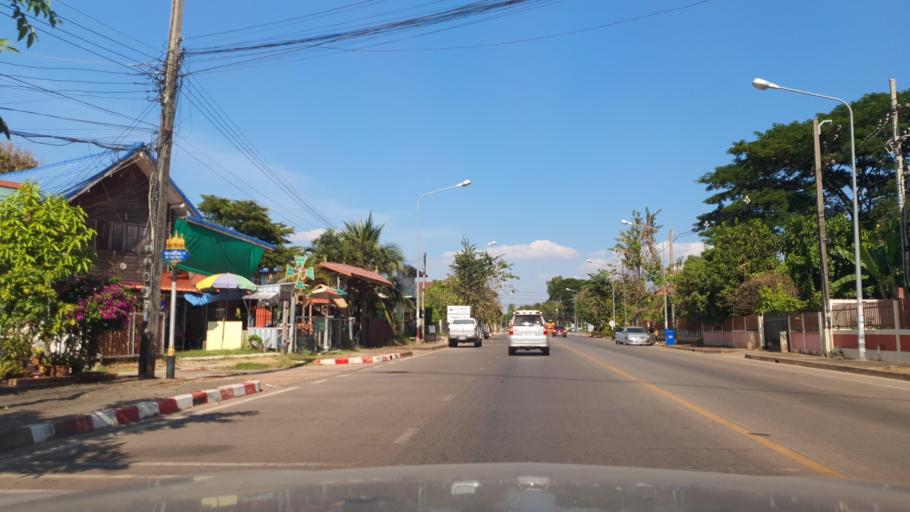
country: TH
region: Sakon Nakhon
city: Sakon Nakhon
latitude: 17.1597
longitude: 104.1267
